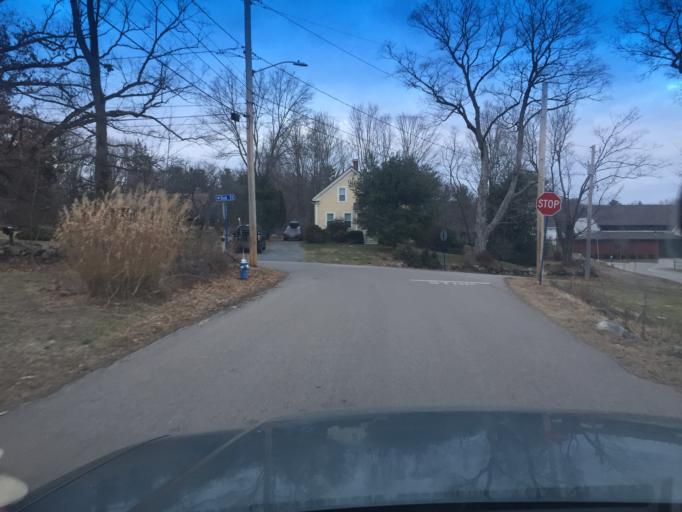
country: US
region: Massachusetts
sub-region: Norfolk County
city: Medway
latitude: 42.1469
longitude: -71.4297
